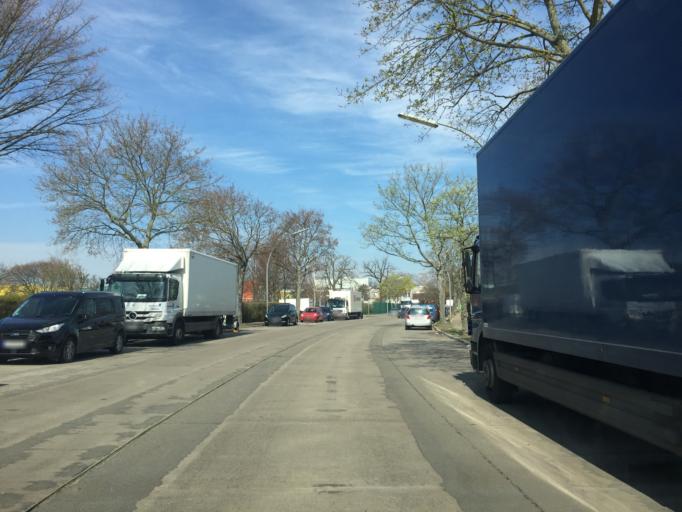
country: DE
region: Berlin
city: Charlottenburg-Nord
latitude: 52.5427
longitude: 13.3134
